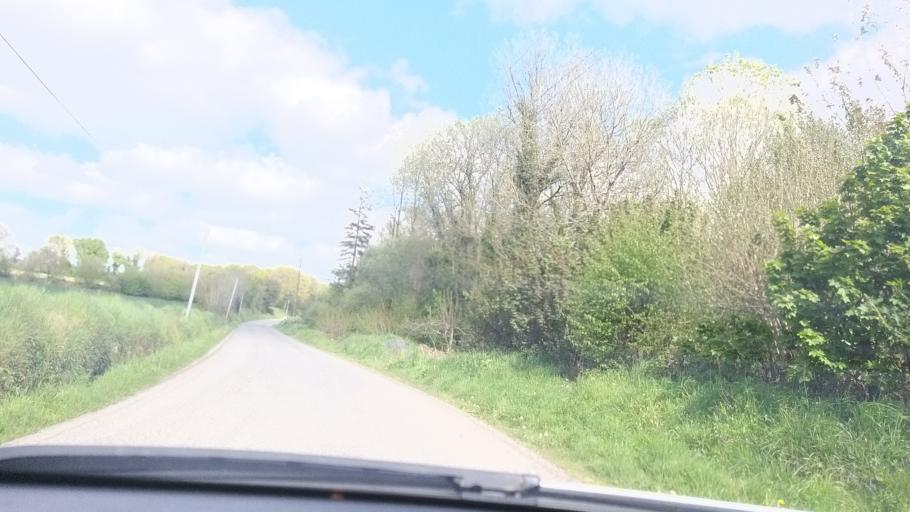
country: FR
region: Brittany
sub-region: Departement du Finistere
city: Huelgoat
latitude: 48.3532
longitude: -3.7096
